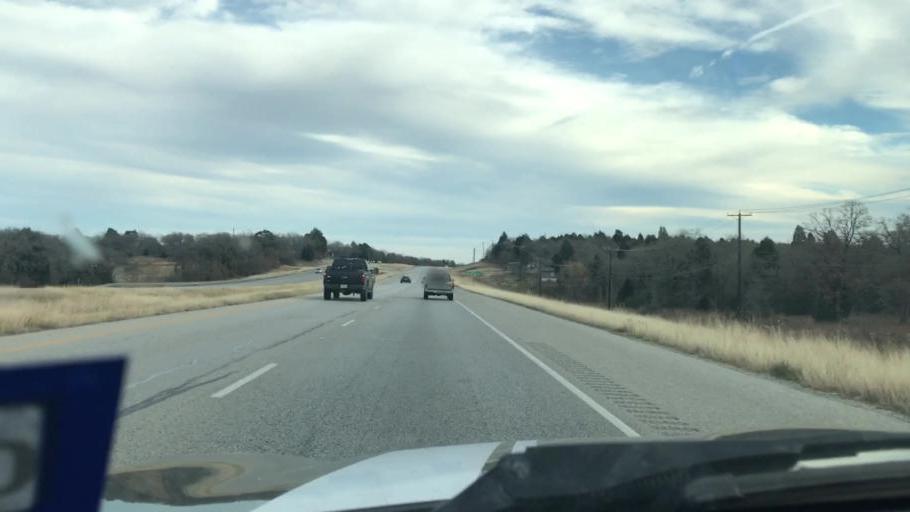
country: US
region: Texas
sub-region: Bastrop County
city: Elgin
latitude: 30.3269
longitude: -97.3342
